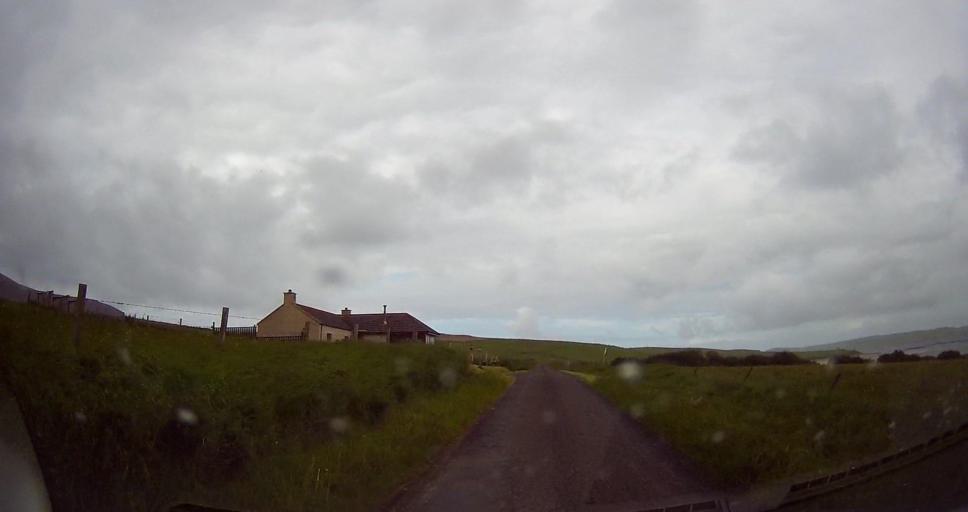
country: GB
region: Scotland
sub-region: Orkney Islands
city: Stromness
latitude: 58.9121
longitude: -3.3212
